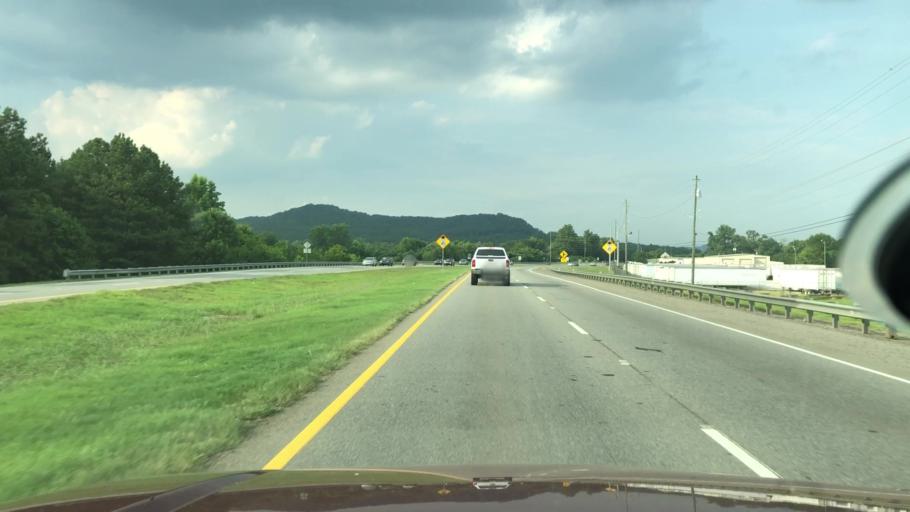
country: US
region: Georgia
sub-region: Bartow County
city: Cartersville
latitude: 34.1380
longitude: -84.8446
